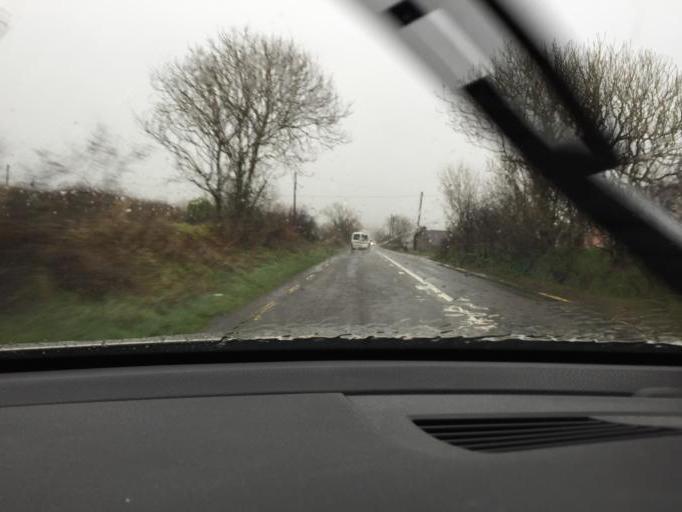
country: IE
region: Munster
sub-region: Ciarrai
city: Dingle
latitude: 52.1405
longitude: -10.2060
